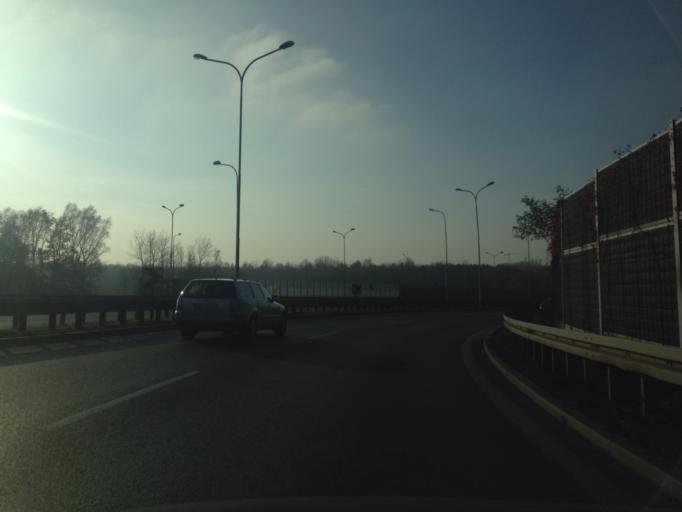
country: PL
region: Silesian Voivodeship
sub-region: Katowice
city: Katowice
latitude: 50.2428
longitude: 19.0490
